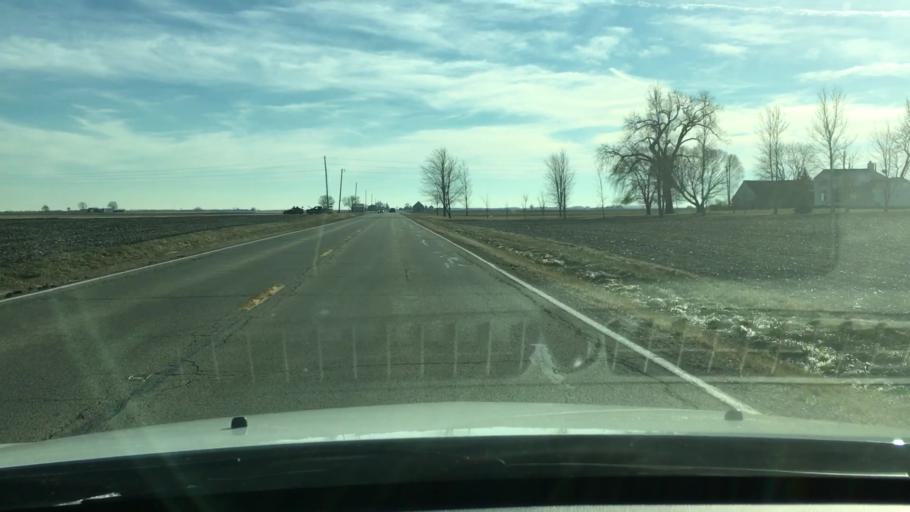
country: US
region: Illinois
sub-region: LaSalle County
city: Peru
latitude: 41.4272
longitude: -89.1265
